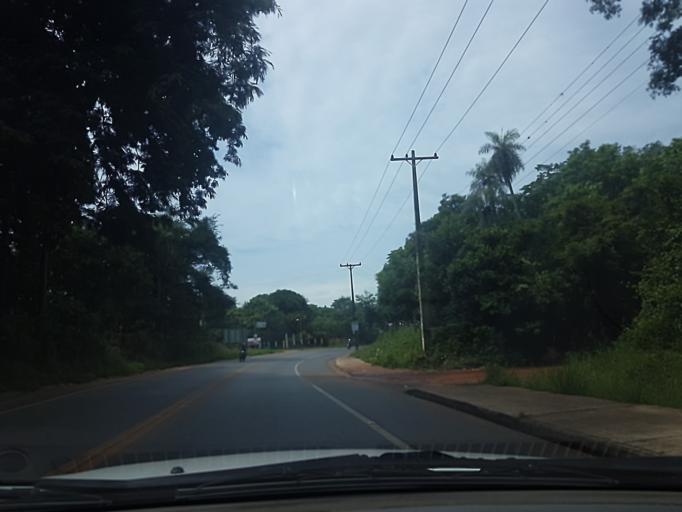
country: PY
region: Central
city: Limpio
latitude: -25.2421
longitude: -57.4581
